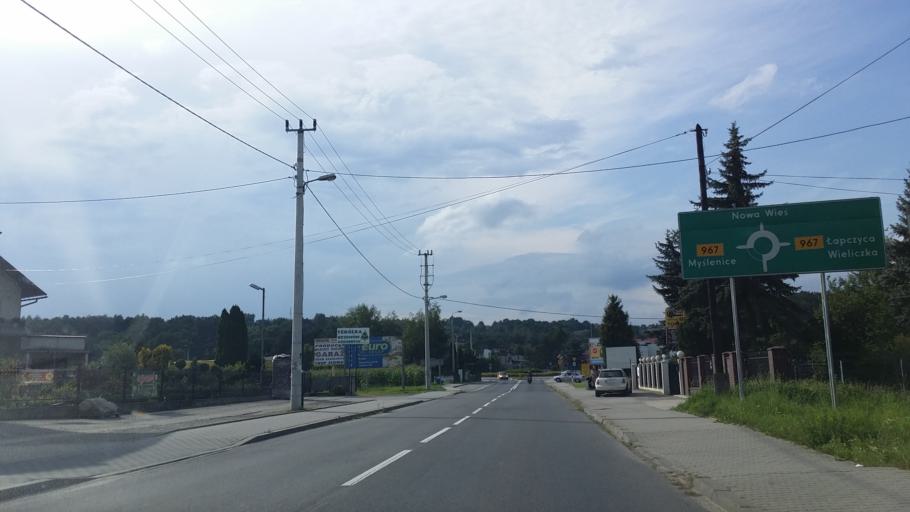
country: PL
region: Lesser Poland Voivodeship
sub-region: Powiat myslenicki
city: Dobczyce
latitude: 49.8858
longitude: 20.0809
